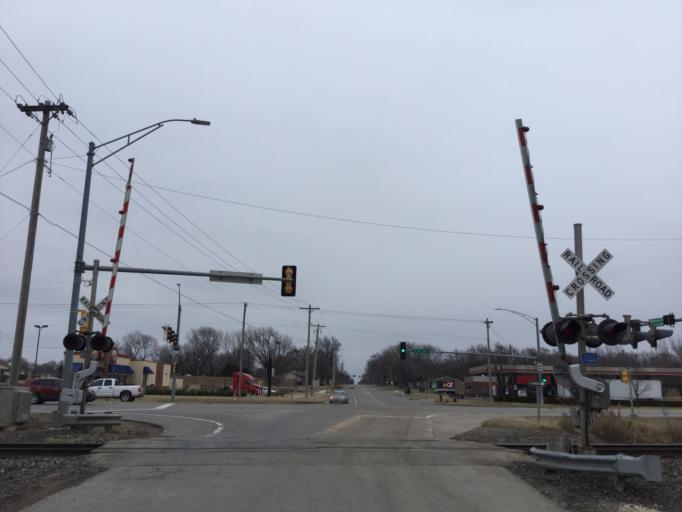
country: US
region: Kansas
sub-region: Sedgwick County
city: Derby
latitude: 37.5625
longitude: -97.2768
